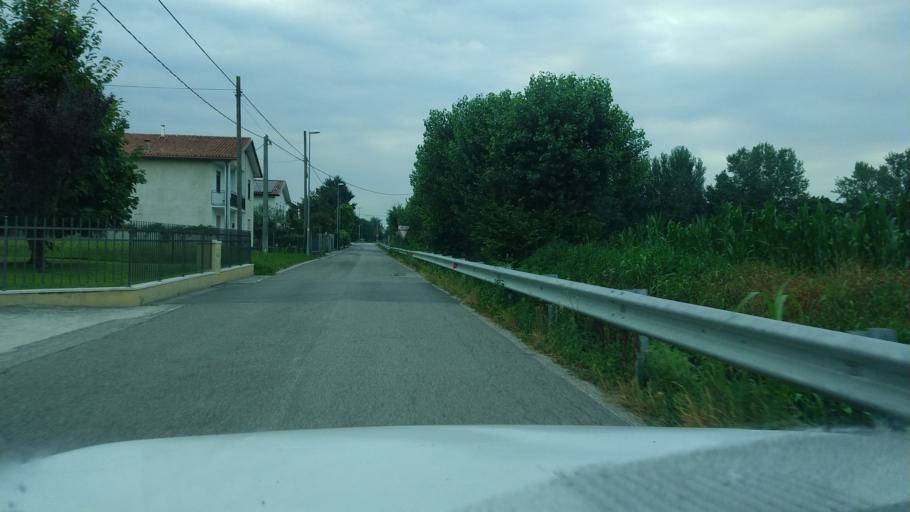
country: IT
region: Veneto
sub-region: Provincia di Vicenza
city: Schiavon
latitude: 45.7114
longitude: 11.6468
